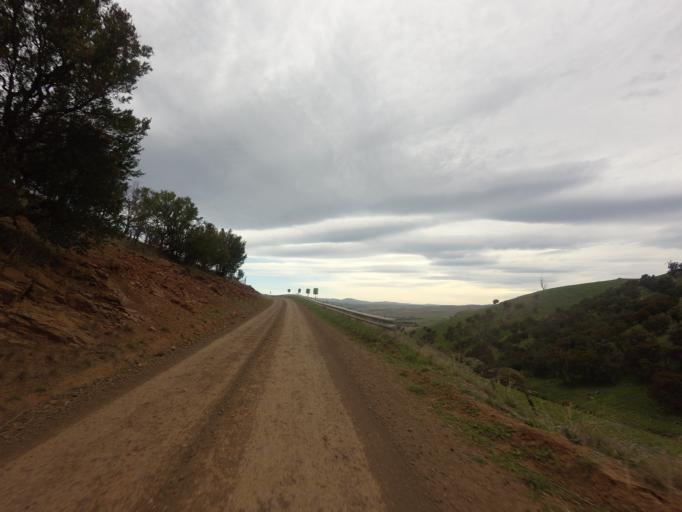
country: AU
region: Tasmania
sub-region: Derwent Valley
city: New Norfolk
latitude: -42.4543
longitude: 146.7662
